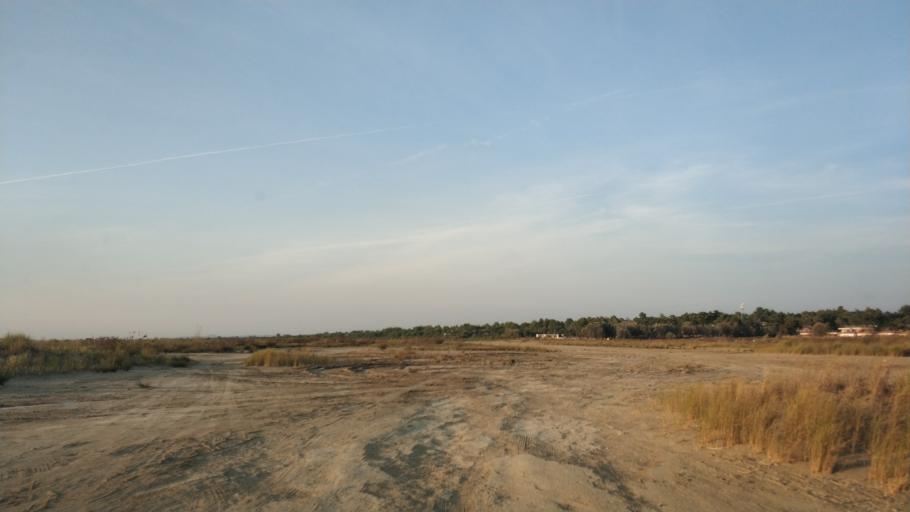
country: AL
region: Fier
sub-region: Rrethi i Lushnjes
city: Divjake
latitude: 40.9689
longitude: 19.4757
